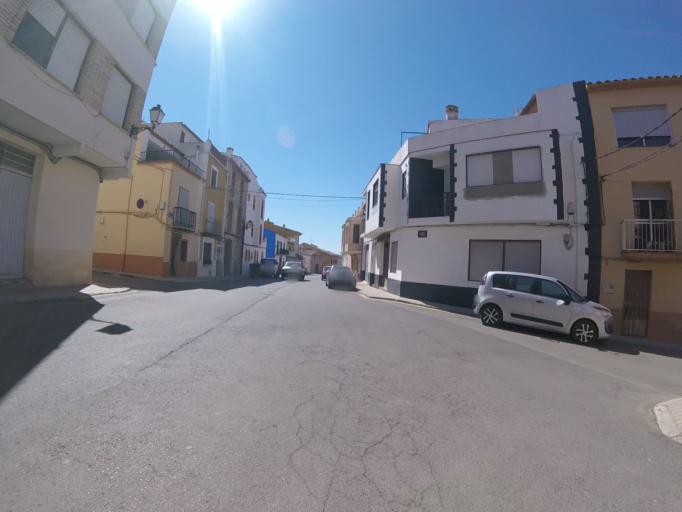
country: ES
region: Valencia
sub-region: Provincia de Castello
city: Chert/Xert
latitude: 40.4173
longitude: 0.1736
